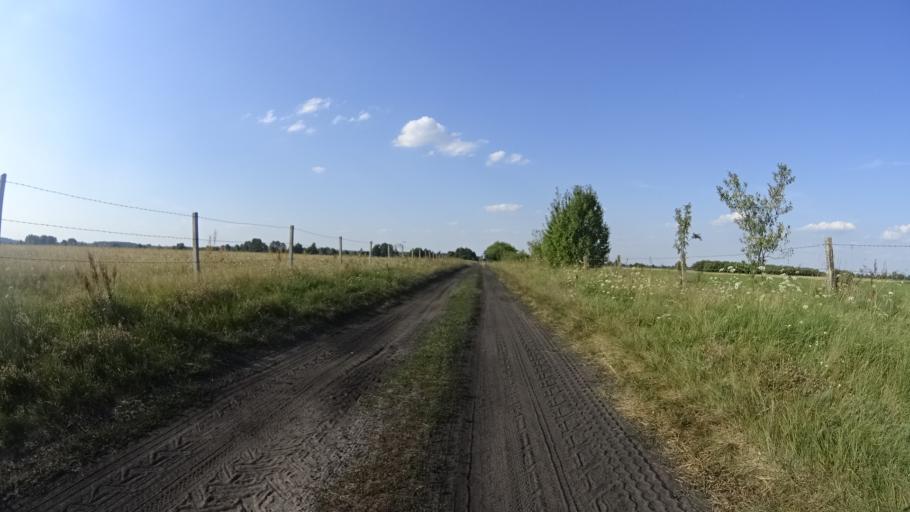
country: PL
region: Masovian Voivodeship
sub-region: Powiat bialobrzeski
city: Wysmierzyce
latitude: 51.6334
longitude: 20.8161
